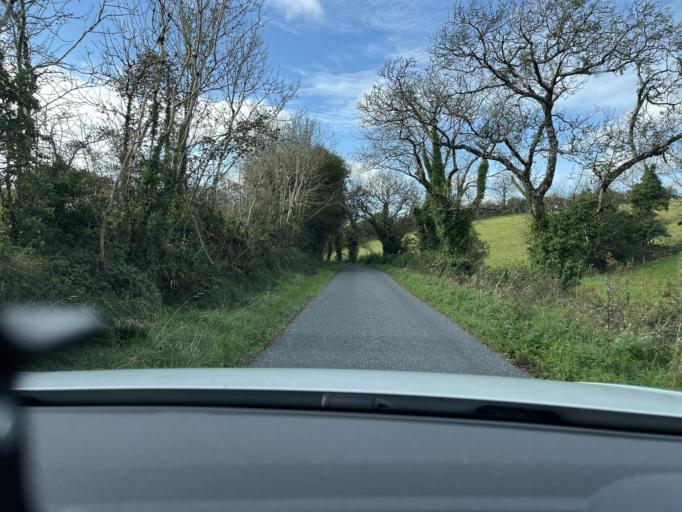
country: IE
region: Connaught
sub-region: Sligo
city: Ballymote
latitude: 54.0769
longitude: -8.4412
